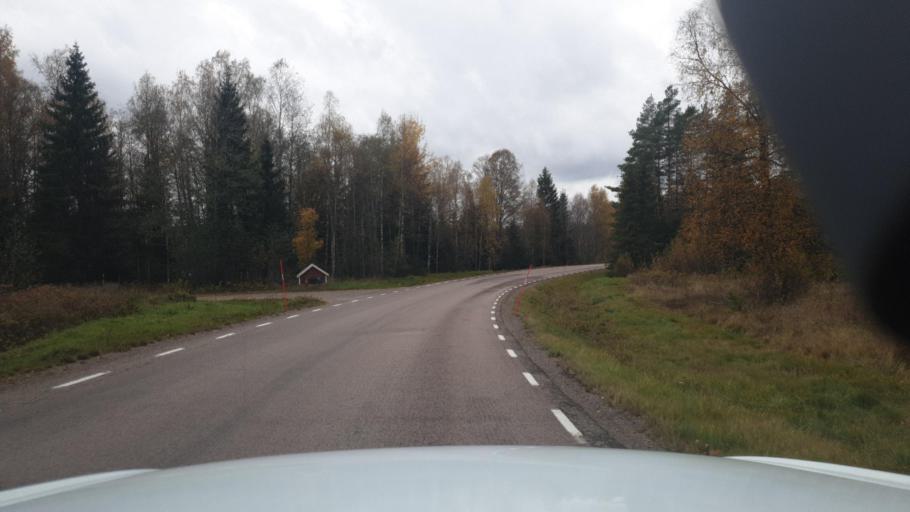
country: SE
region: Vaermland
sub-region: Arvika Kommun
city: Arvika
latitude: 59.9436
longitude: 12.6896
